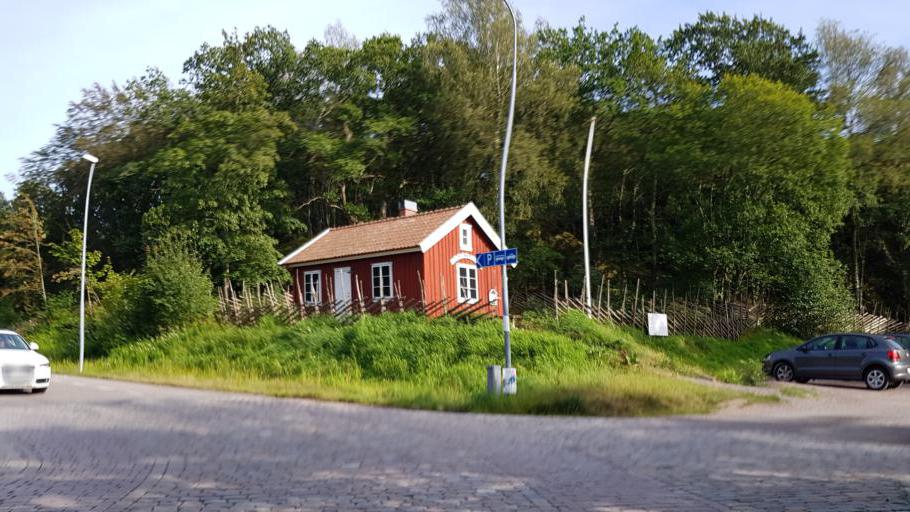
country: SE
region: Vaestra Goetaland
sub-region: Molndal
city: Moelndal
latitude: 57.6627
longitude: 12.0503
